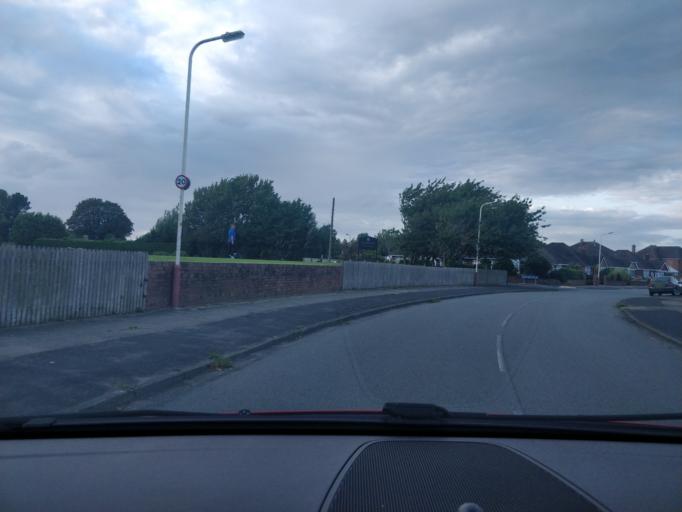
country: GB
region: England
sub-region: Sefton
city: Southport
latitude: 53.6607
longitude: -2.9782
